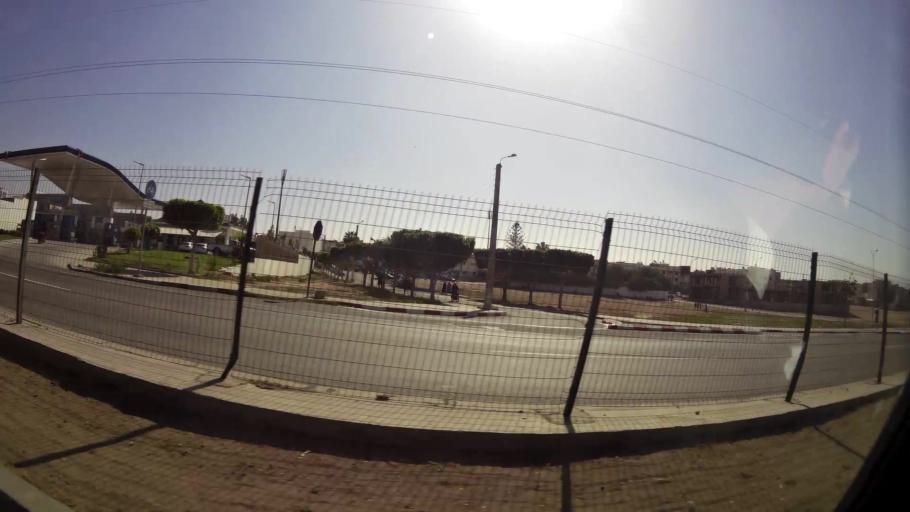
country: MA
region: Souss-Massa-Draa
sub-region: Inezgane-Ait Mellou
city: Inezgane
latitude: 30.3772
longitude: -9.5048
